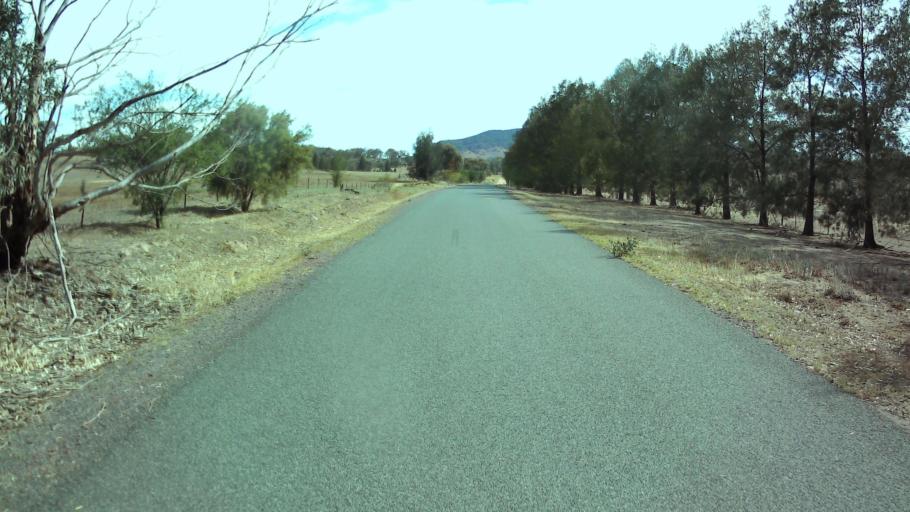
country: AU
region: New South Wales
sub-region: Weddin
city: Grenfell
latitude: -33.8108
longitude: 148.2928
